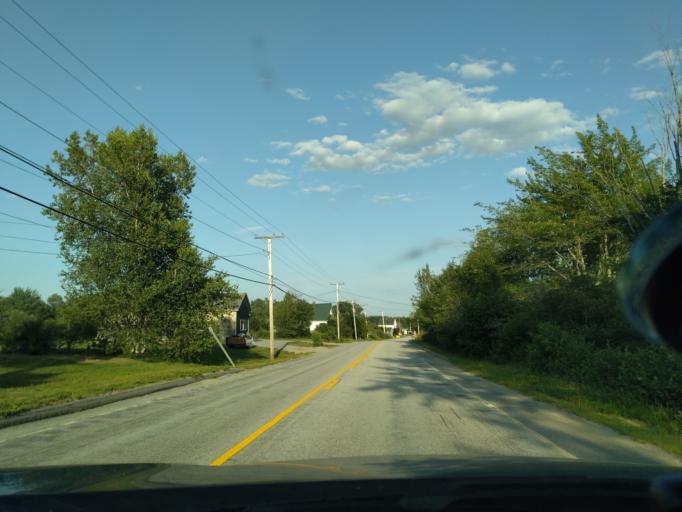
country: US
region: Maine
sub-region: Hancock County
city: Gouldsboro
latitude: 44.3906
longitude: -68.0447
